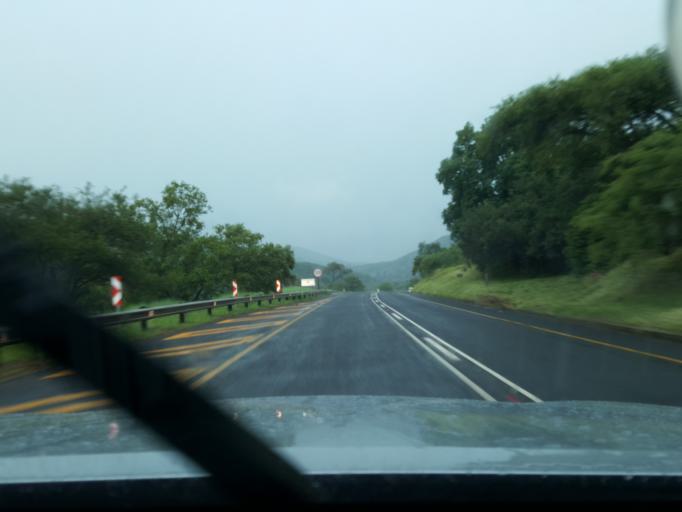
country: ZA
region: Mpumalanga
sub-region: Ehlanzeni District
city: Nelspruit
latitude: -25.5700
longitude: 30.6695
